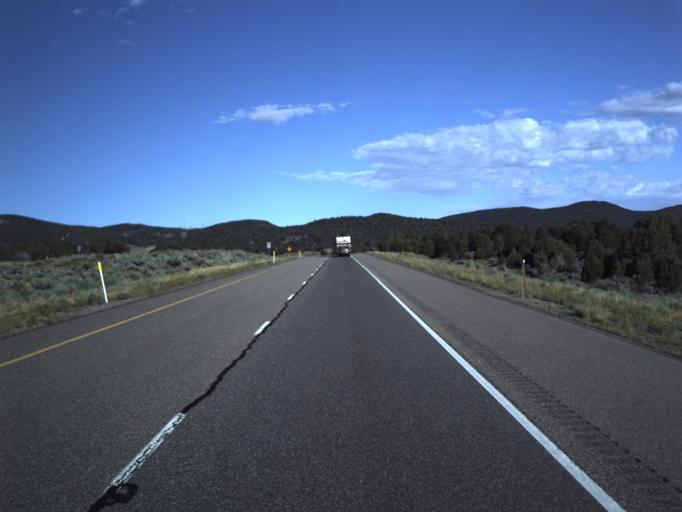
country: US
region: Utah
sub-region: Sevier County
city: Monroe
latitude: 38.5706
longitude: -112.4502
